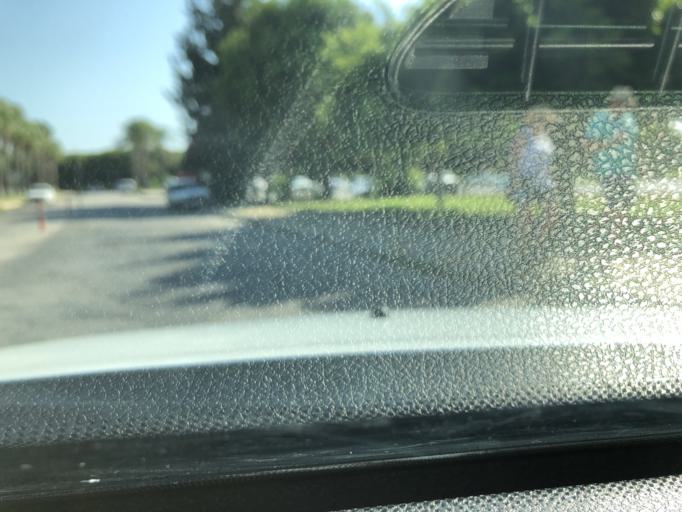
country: TR
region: Antalya
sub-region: Manavgat
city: Side
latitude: 36.7720
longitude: 31.3953
